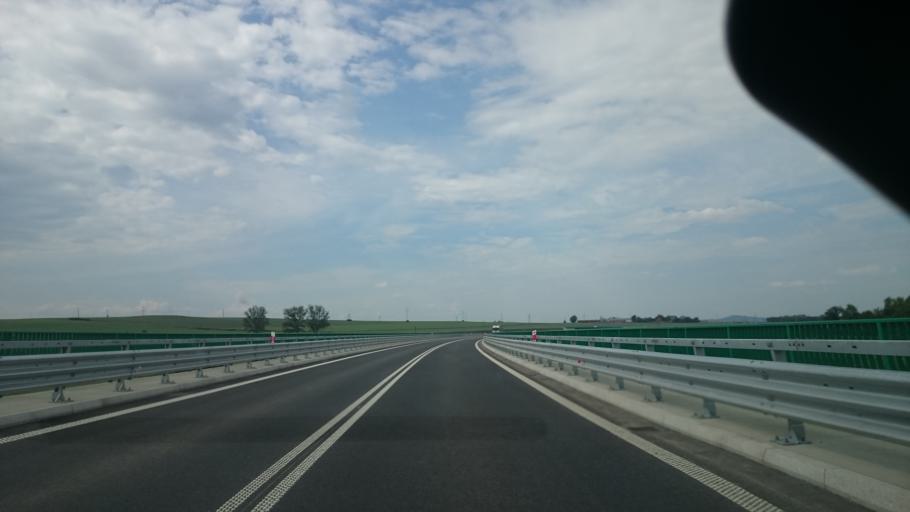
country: PL
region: Lower Silesian Voivodeship
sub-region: Powiat klodzki
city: Klodzko
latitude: 50.4139
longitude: 16.6266
